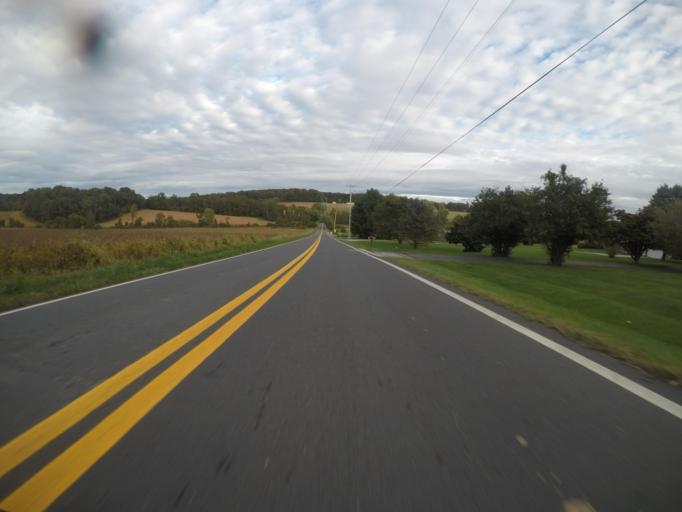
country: US
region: Maryland
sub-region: Carroll County
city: Hampstead
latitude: 39.5695
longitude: -76.8697
